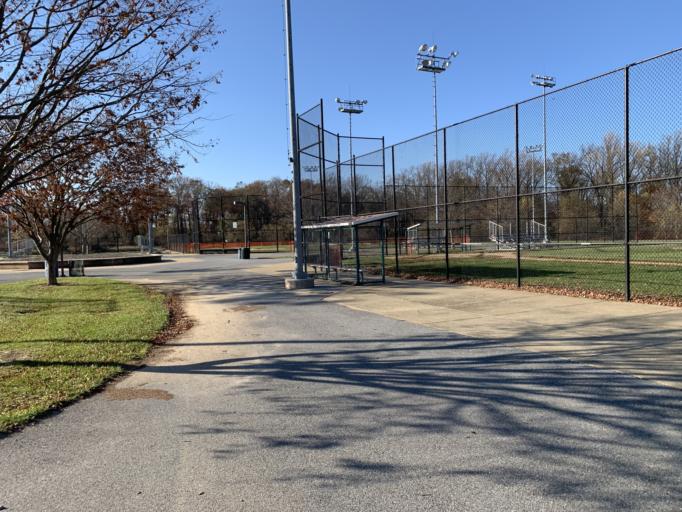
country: US
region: Maryland
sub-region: Baltimore County
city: Reisterstown
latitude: 39.4713
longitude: -76.8469
